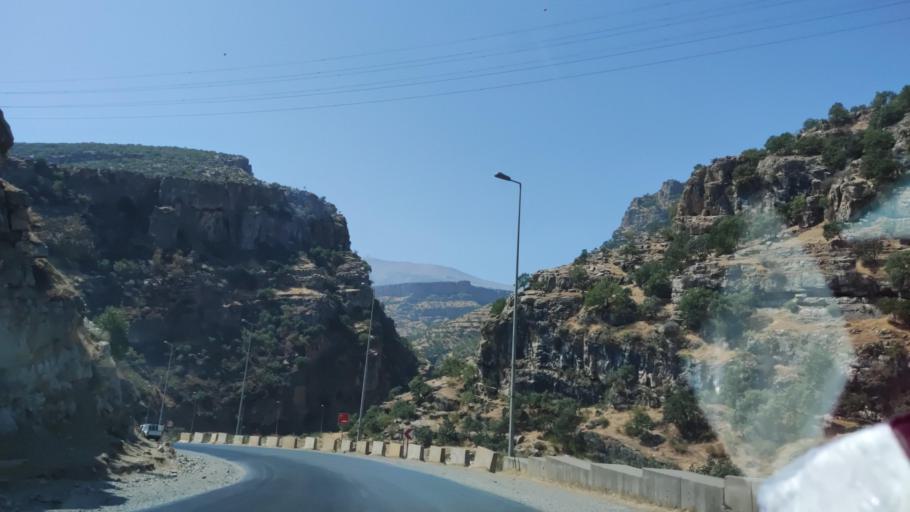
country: IQ
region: Arbil
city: Ruwandiz
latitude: 36.6471
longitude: 44.4968
